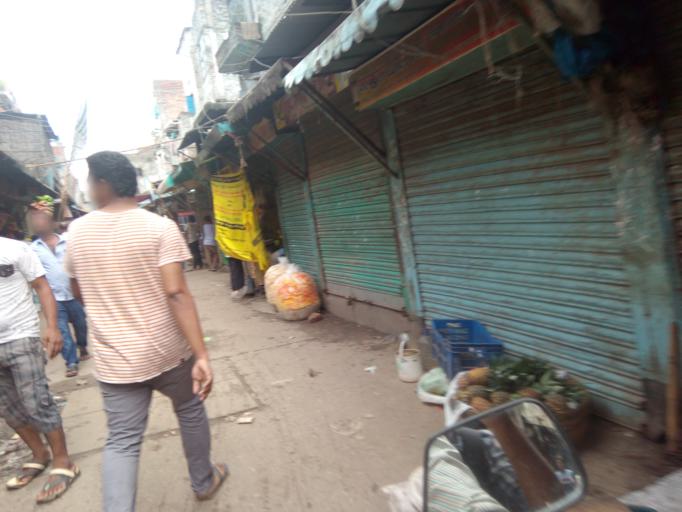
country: BD
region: Dhaka
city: Azimpur
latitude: 23.7679
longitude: 90.3662
